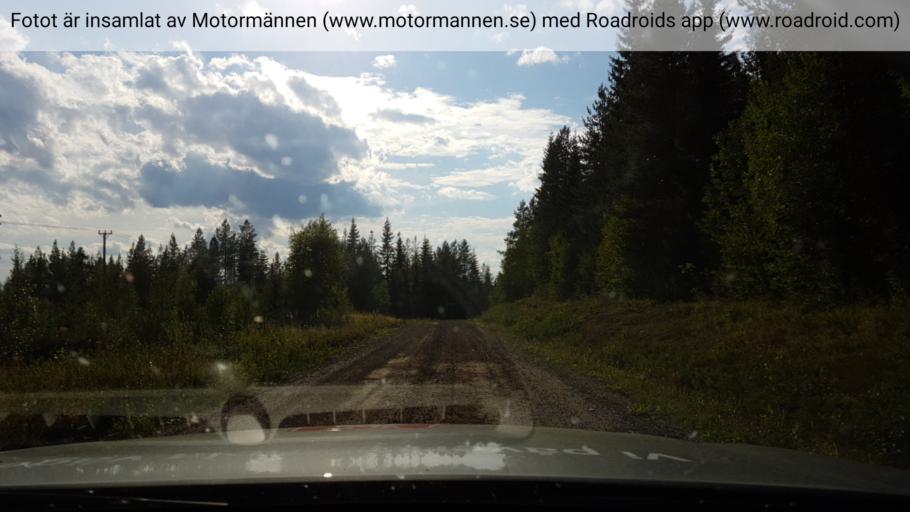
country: SE
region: Jaemtland
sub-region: Stroemsunds Kommun
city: Stroemsund
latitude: 63.7207
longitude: 16.0475
